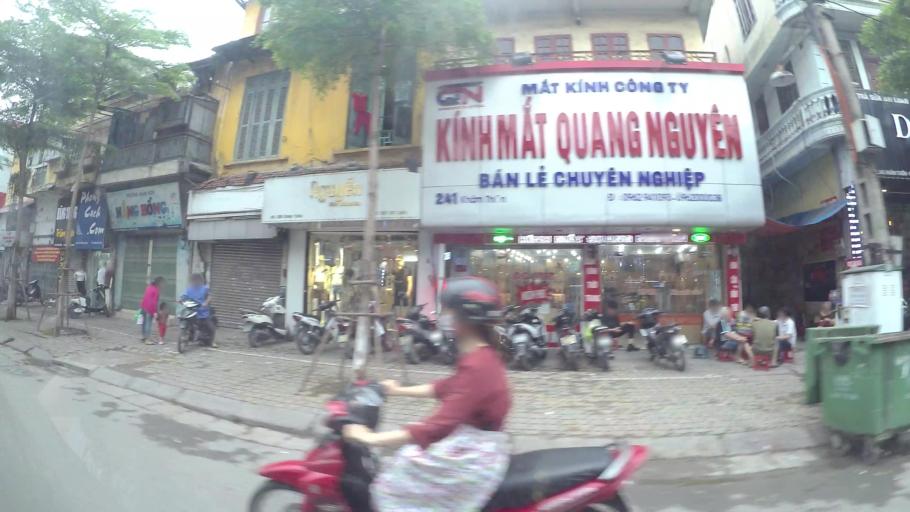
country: VN
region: Ha Noi
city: Dong Da
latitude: 21.0195
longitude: 105.8321
